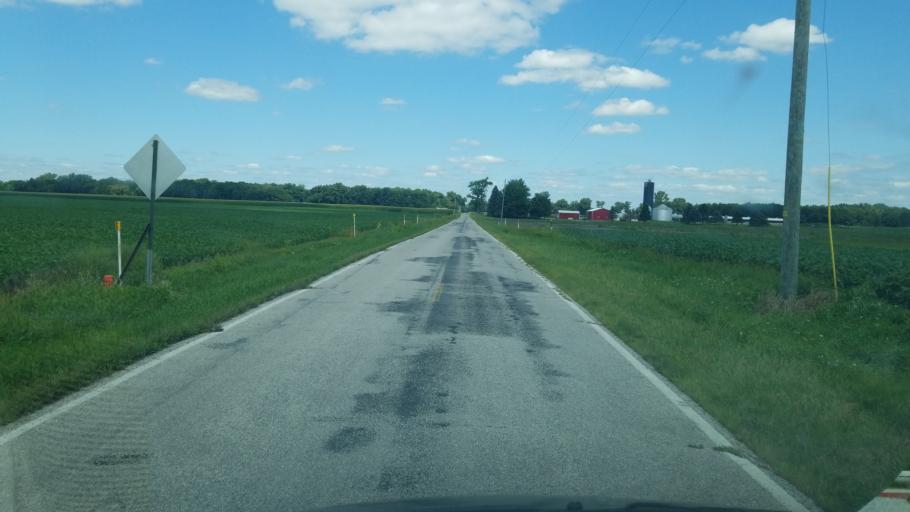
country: US
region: Ohio
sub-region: Fulton County
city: Delta
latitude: 41.6193
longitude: -84.0151
